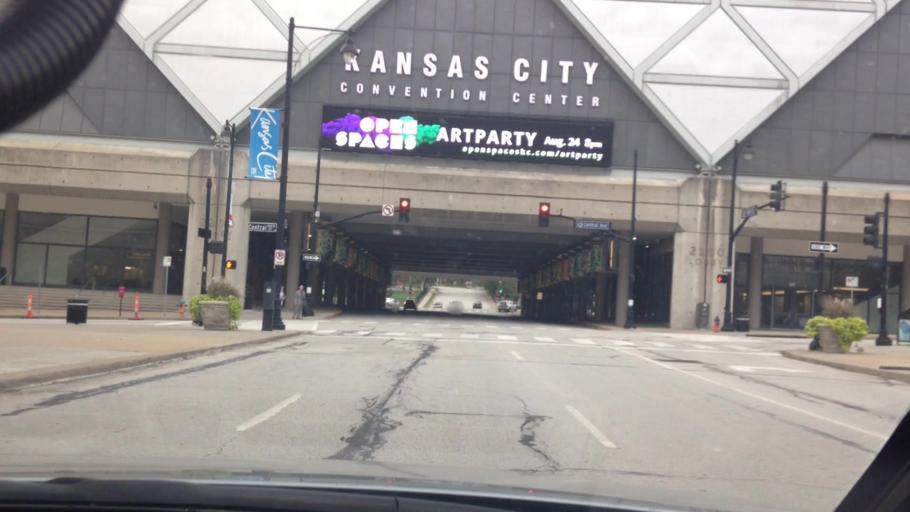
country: US
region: Missouri
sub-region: Jackson County
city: Kansas City
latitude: 39.0987
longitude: -94.5867
